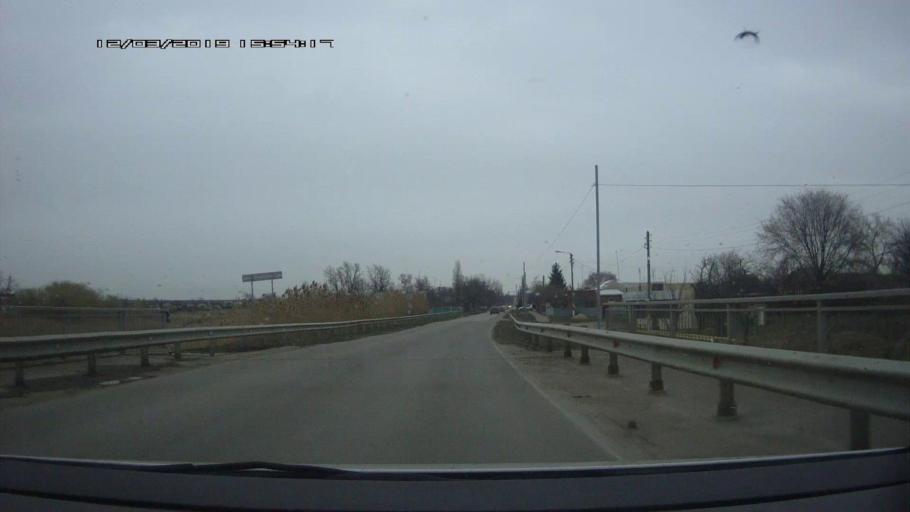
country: RU
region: Rostov
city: Novobataysk
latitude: 46.8897
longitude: 39.7772
